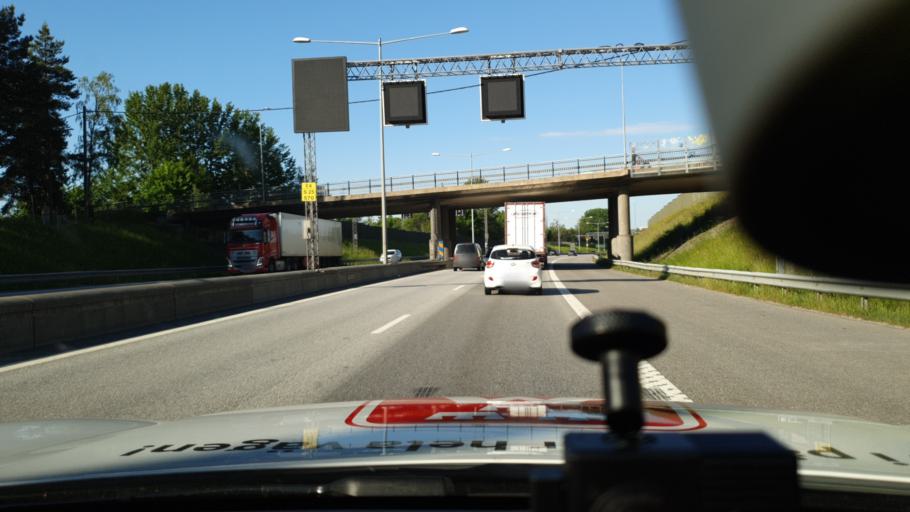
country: SE
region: Stockholm
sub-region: Sodertalje Kommun
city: Soedertaelje
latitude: 59.1921
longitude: 17.6564
